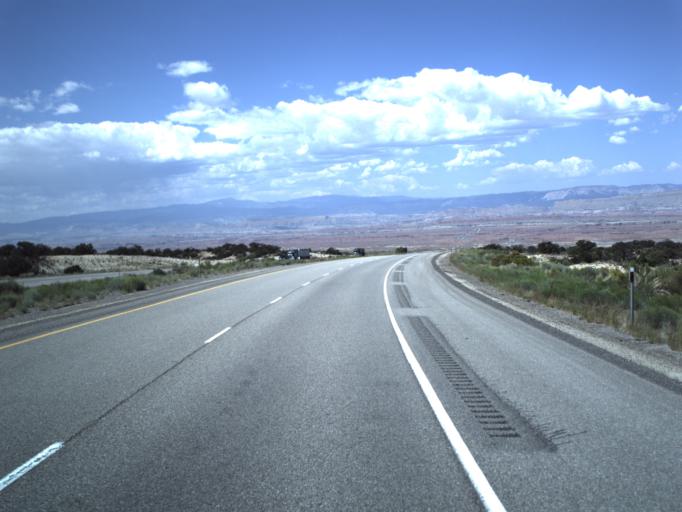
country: US
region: Utah
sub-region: Emery County
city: Ferron
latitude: 38.8477
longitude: -110.9345
